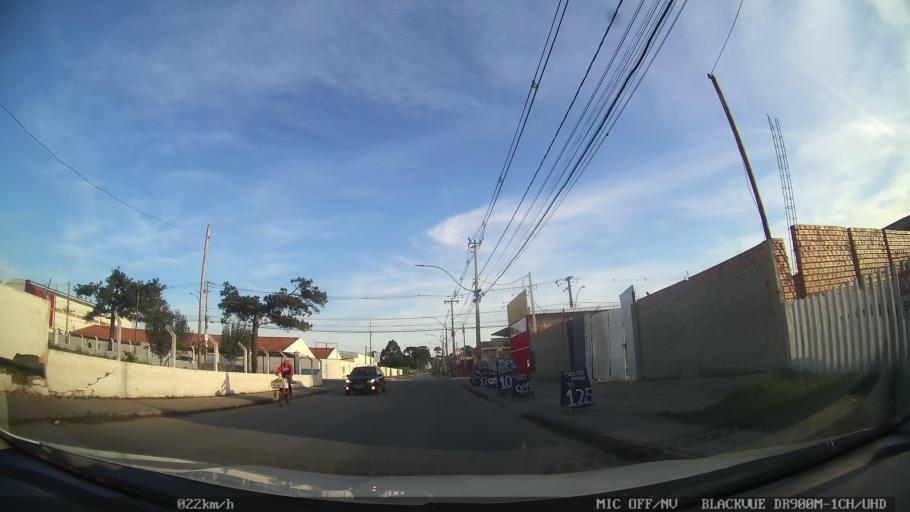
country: BR
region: Parana
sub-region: Pinhais
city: Pinhais
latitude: -25.4592
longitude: -49.1475
